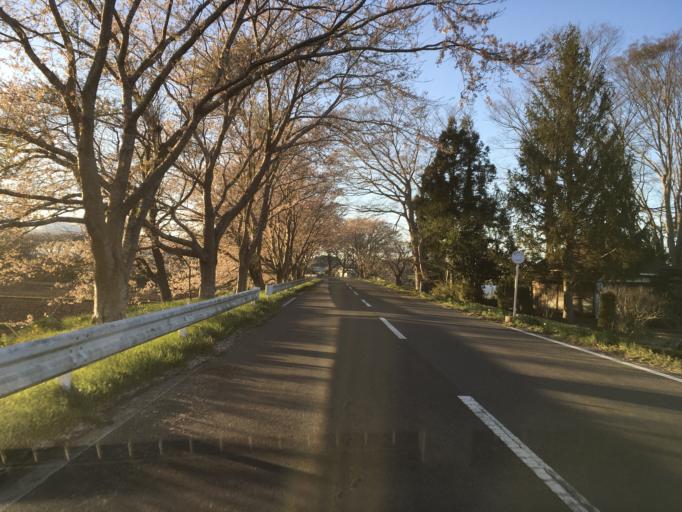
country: JP
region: Miyagi
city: Wakuya
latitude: 38.6469
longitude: 141.1607
